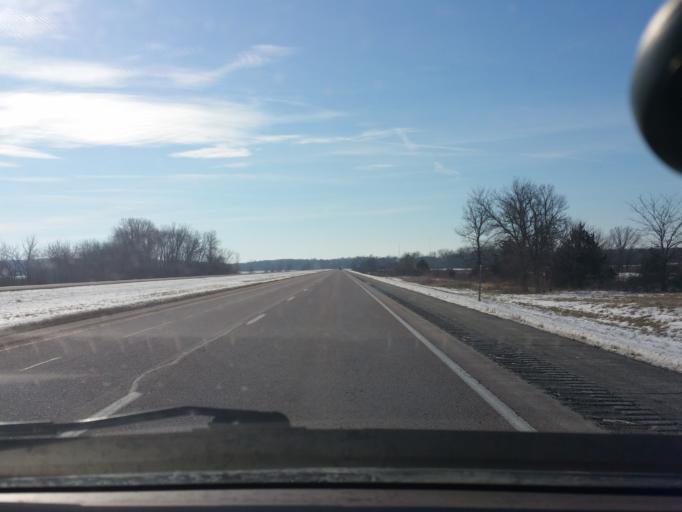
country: US
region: Iowa
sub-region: Decatur County
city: Lamoni
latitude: 40.6781
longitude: -93.8488
